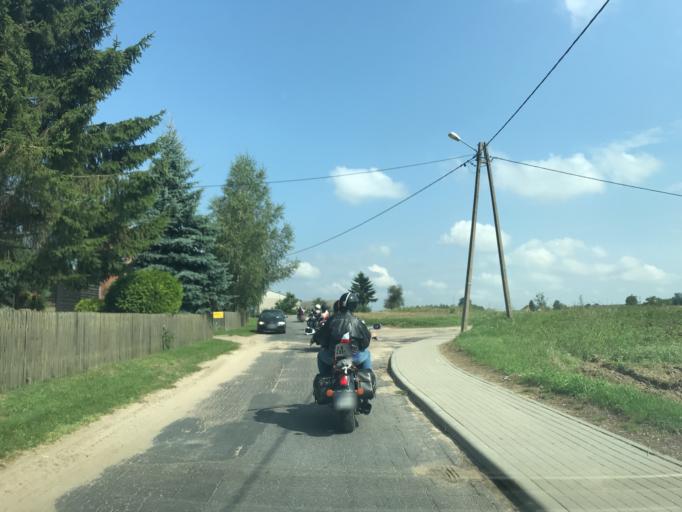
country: PL
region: Warmian-Masurian Voivodeship
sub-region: Powiat nowomiejski
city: Biskupiec
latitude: 53.4222
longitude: 19.4425
